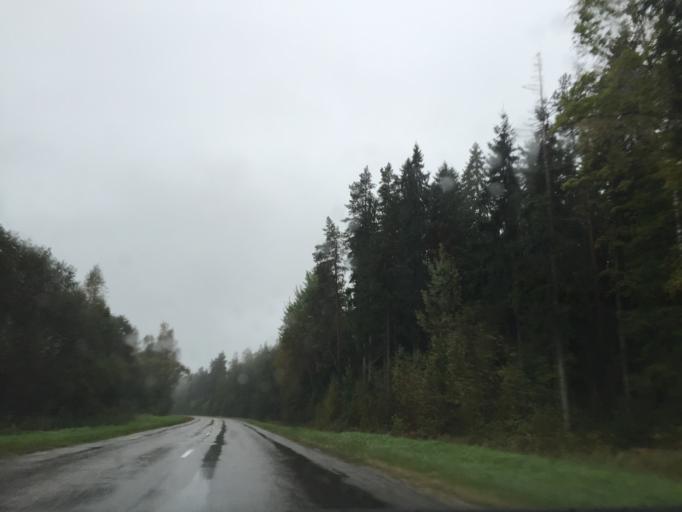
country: LV
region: Incukalns
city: Incukalns
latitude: 57.0276
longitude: 24.6824
